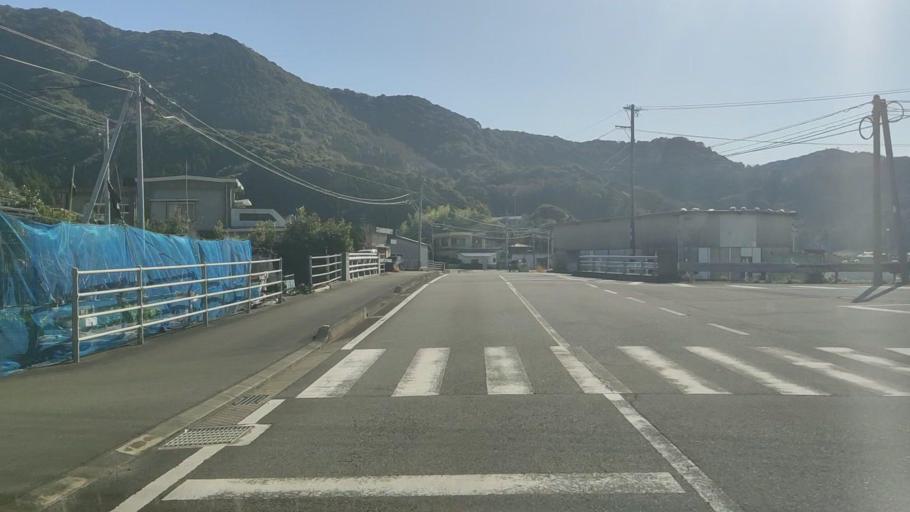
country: JP
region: Oita
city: Saiki
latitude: 32.8031
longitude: 131.8990
